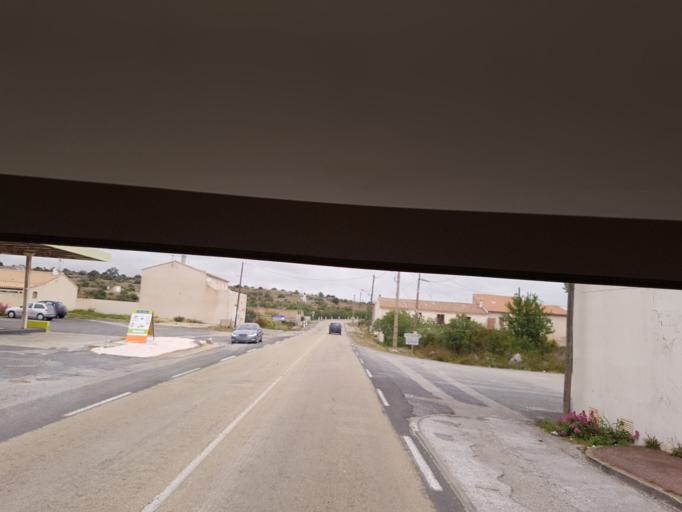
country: FR
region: Languedoc-Roussillon
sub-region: Departement de l'Aude
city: Leucate
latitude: 42.8979
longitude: 2.9984
